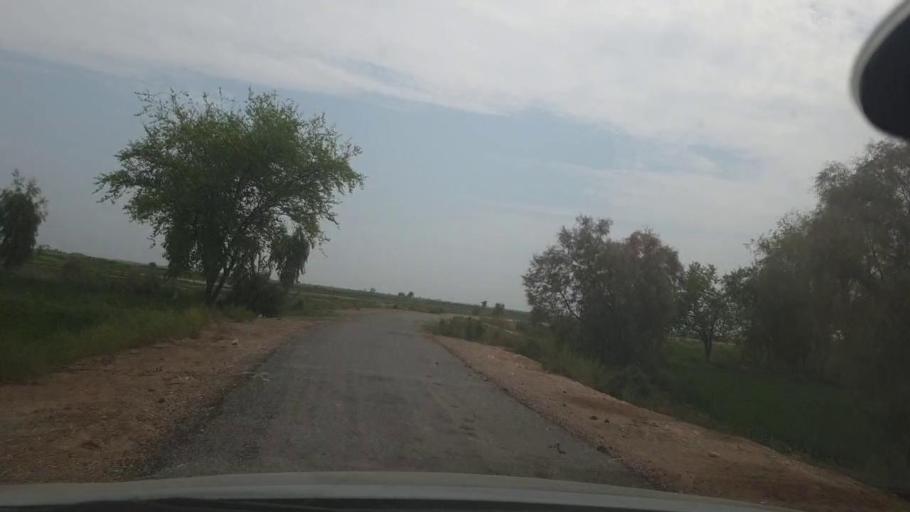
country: PK
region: Balochistan
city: Garhi Khairo
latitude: 28.0225
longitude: 68.0442
